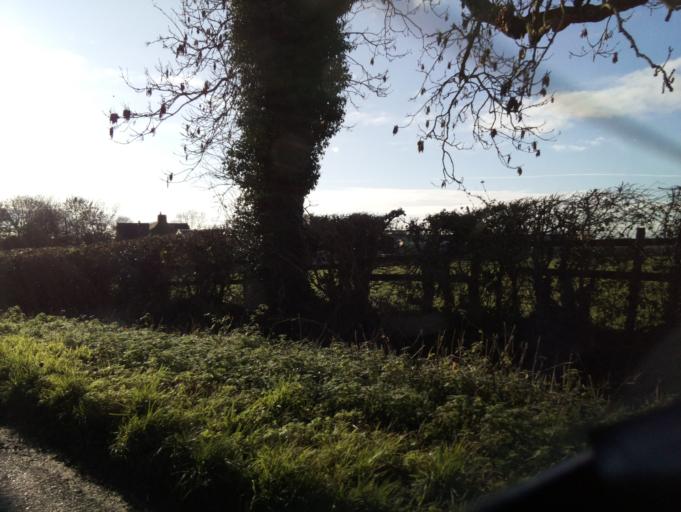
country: GB
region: England
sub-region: Derbyshire
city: Etwall
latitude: 52.8655
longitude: -1.6018
